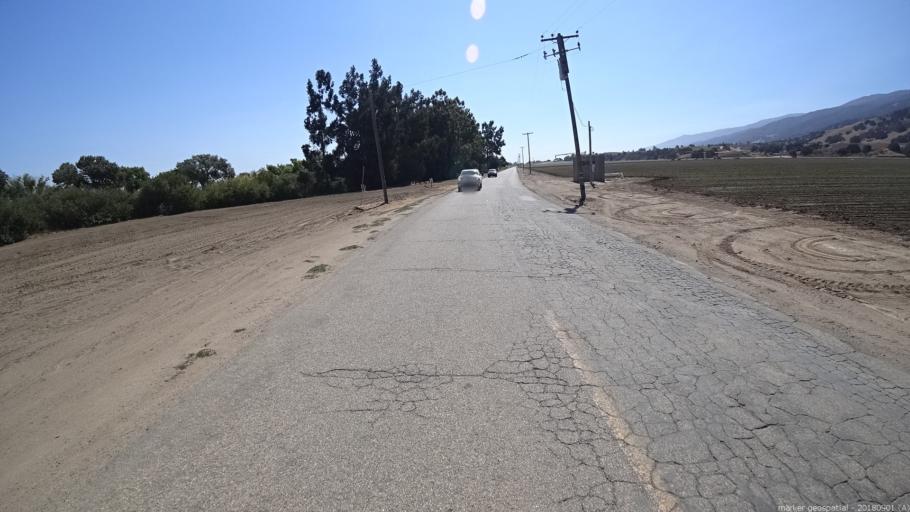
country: US
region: California
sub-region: Monterey County
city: Chualar
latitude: 36.5326
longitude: -121.5352
